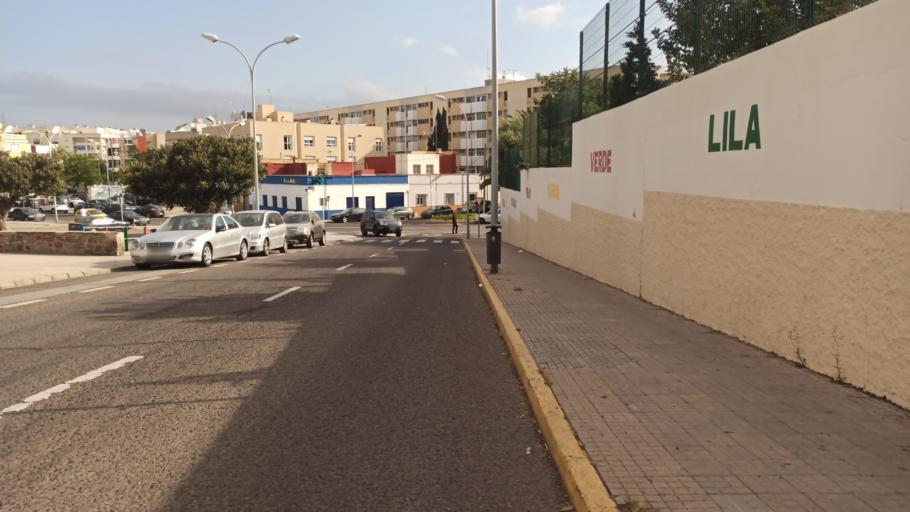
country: ES
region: Melilla
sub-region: Melilla
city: Melilla
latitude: 35.2858
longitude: -2.9505
